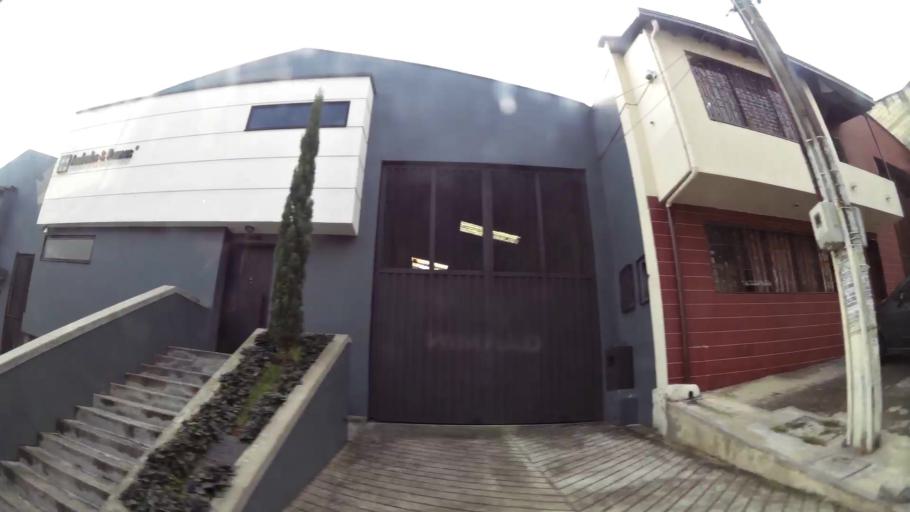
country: CO
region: Antioquia
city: Sabaneta
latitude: 6.1665
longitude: -75.6237
